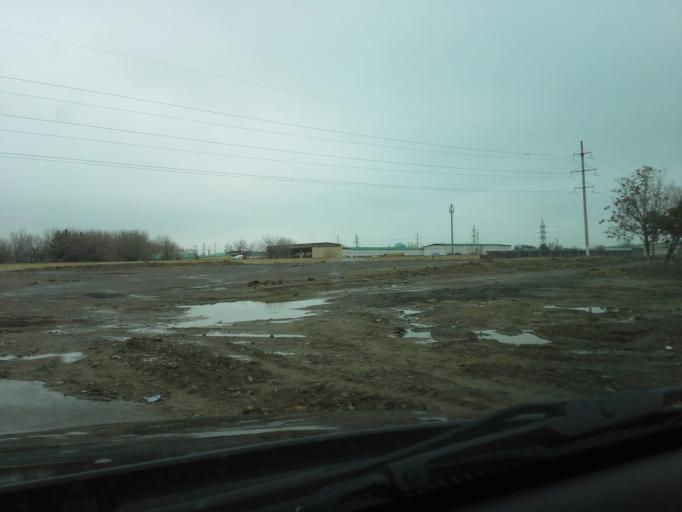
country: TM
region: Ahal
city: Ashgabat
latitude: 37.9521
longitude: 58.4250
